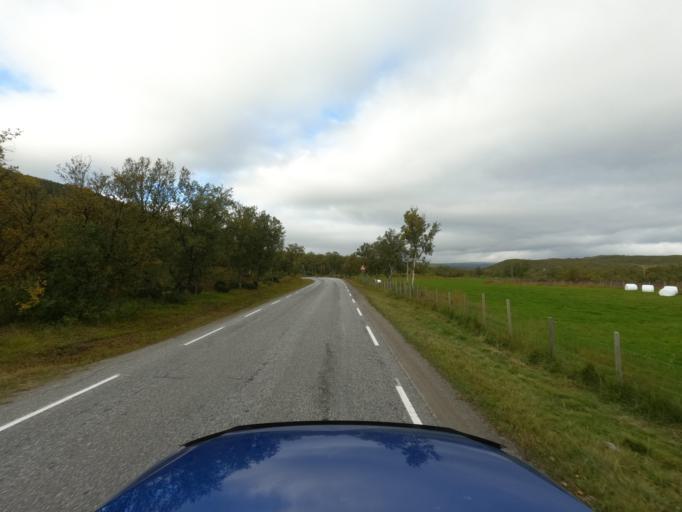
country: NO
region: Finnmark Fylke
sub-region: Porsanger
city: Lakselv
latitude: 70.2980
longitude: 25.0679
